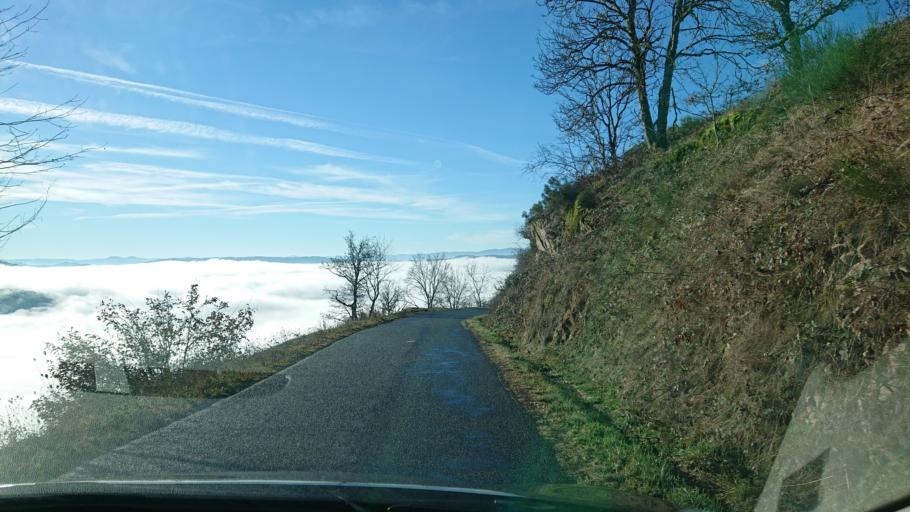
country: FR
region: Auvergne
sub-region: Departement de la Haute-Loire
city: Vorey
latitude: 45.2128
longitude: 3.9276
